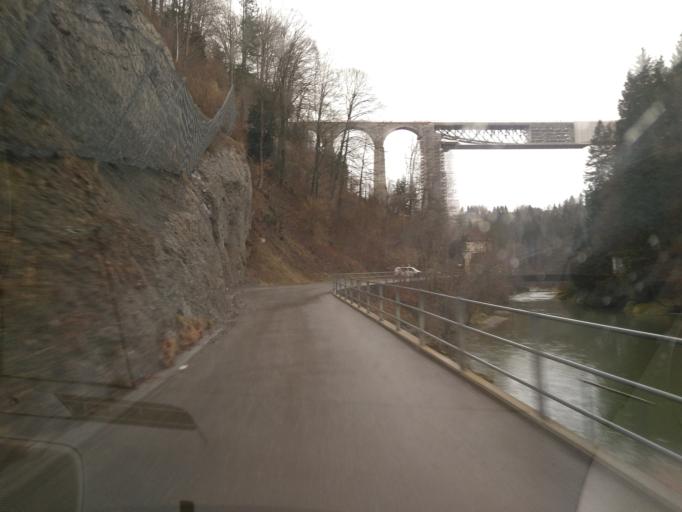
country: CH
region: Appenzell Ausserrhoden
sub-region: Bezirk Hinterland
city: Herisau
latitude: 47.4031
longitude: 9.3231
